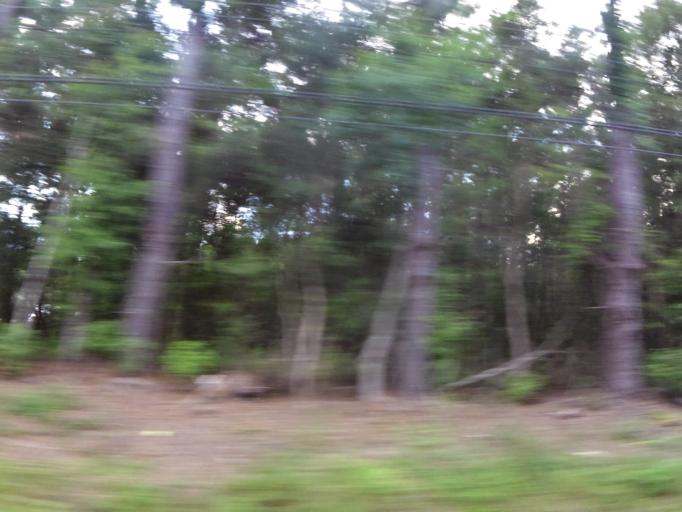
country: US
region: Florida
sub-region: Duval County
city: Jacksonville
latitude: 30.3498
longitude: -81.7728
